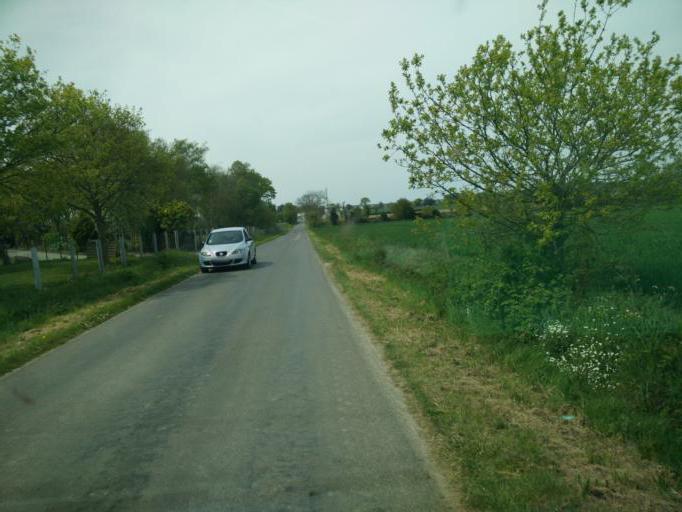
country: FR
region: Brittany
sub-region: Departement des Cotes-d'Armor
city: Matignon
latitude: 48.5912
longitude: -2.2690
